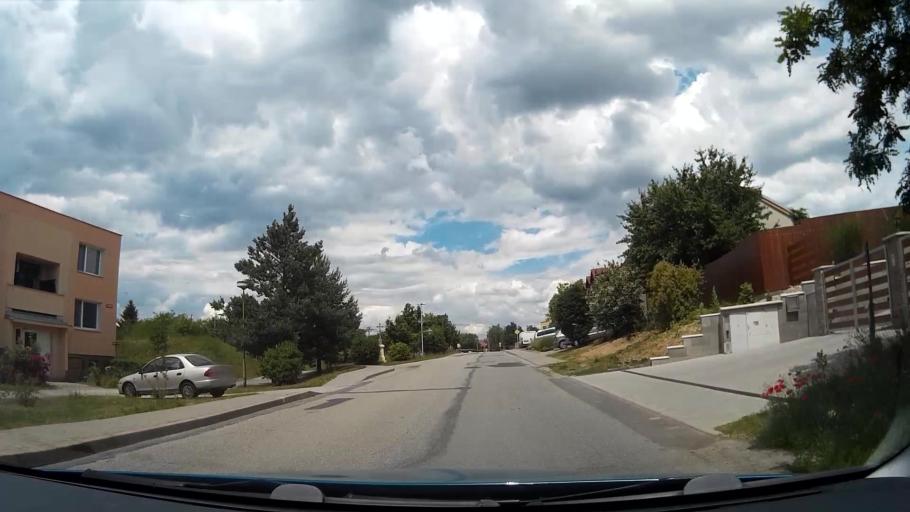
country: CZ
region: South Moravian
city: Orechov
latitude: 49.1156
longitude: 16.5257
